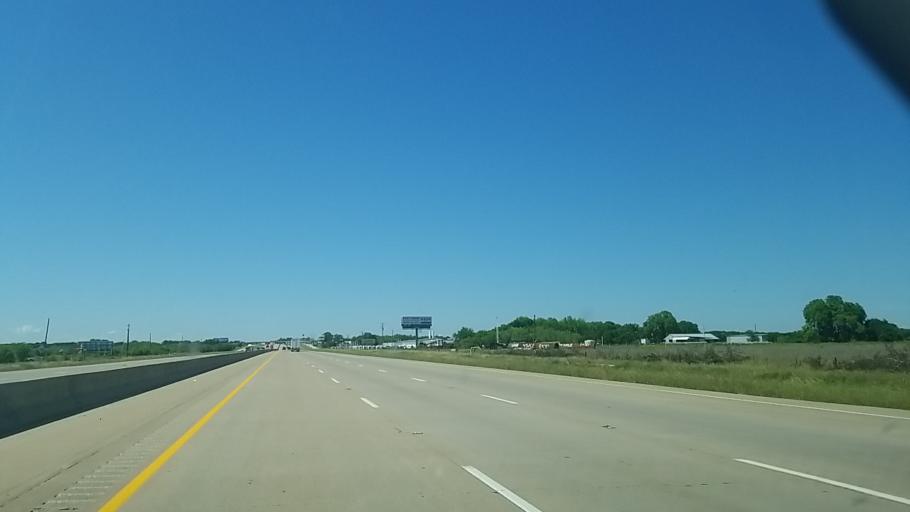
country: US
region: Texas
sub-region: Navarro County
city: Corsicana
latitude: 32.1862
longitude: -96.4721
